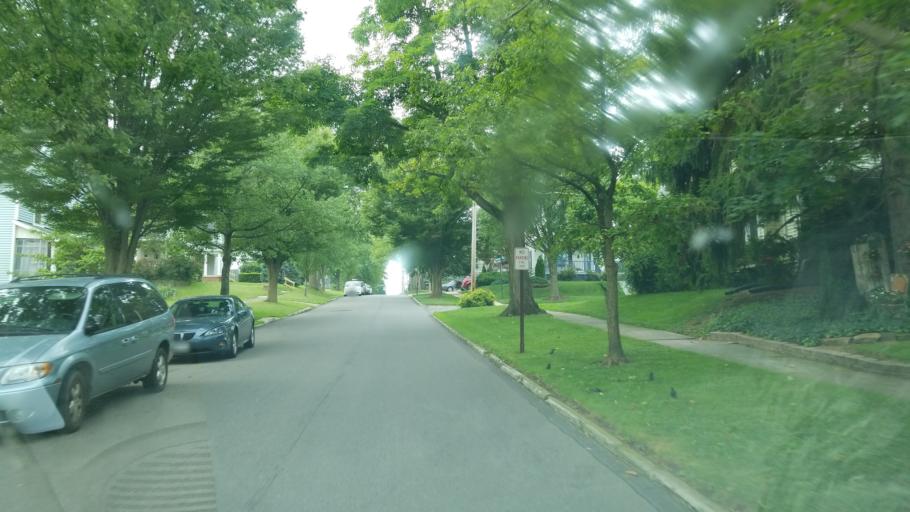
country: US
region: Ohio
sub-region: Ashland County
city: Ashland
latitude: 40.8640
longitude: -82.3078
